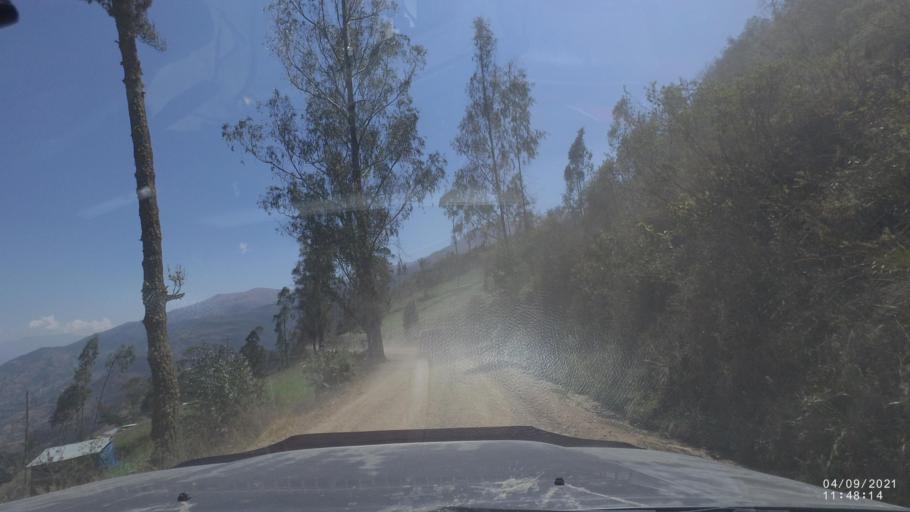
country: BO
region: Cochabamba
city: Colchani
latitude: -17.2253
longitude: -66.5241
